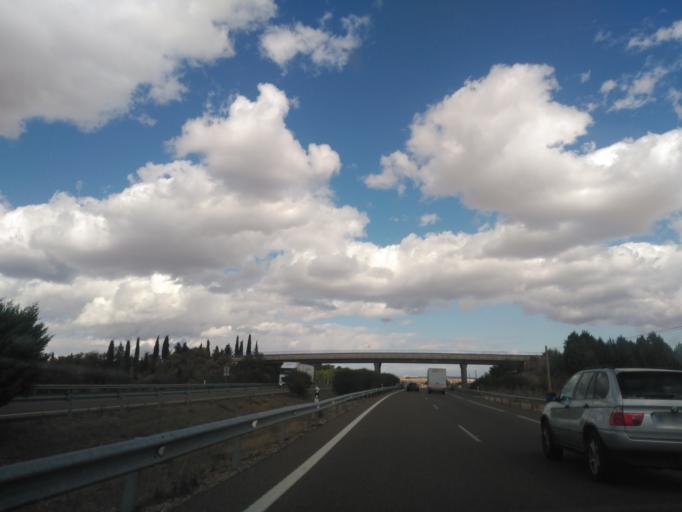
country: ES
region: Castille and Leon
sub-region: Provincia de Palencia
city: Cordovilla la Real
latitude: 42.0530
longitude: -4.2473
